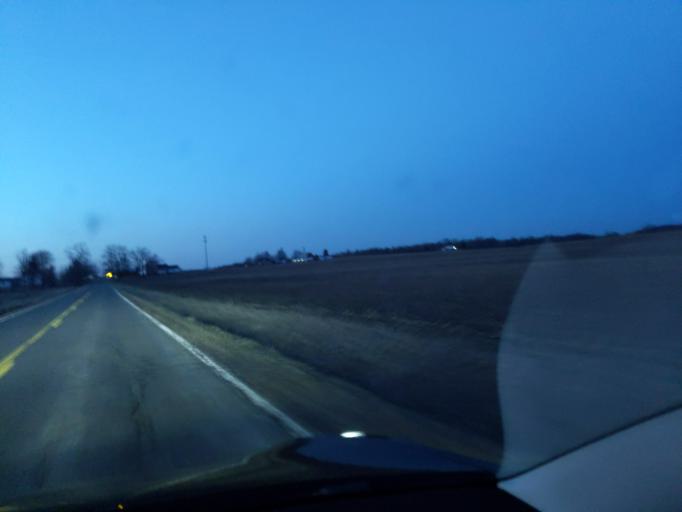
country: US
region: Michigan
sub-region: Ingham County
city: Stockbridge
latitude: 42.5465
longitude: -84.2212
